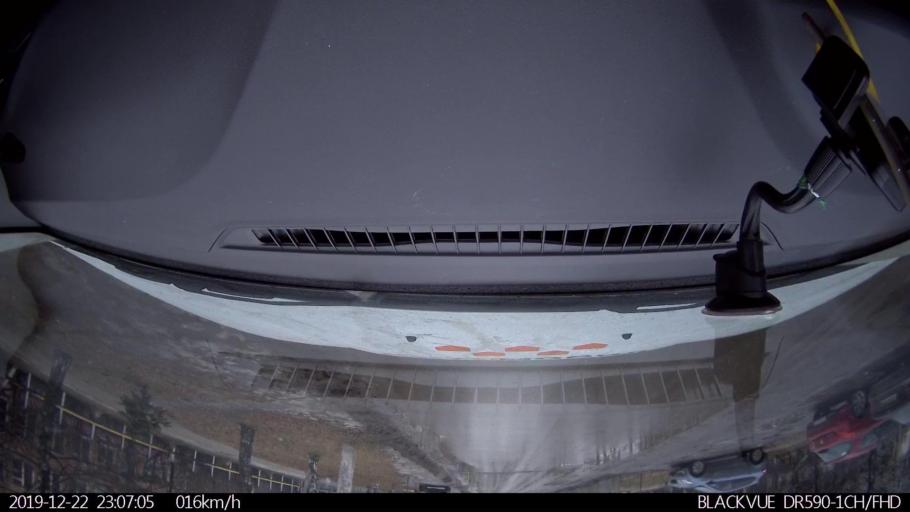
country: RU
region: Nizjnij Novgorod
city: Gorbatovka
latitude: 56.2616
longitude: 43.8597
